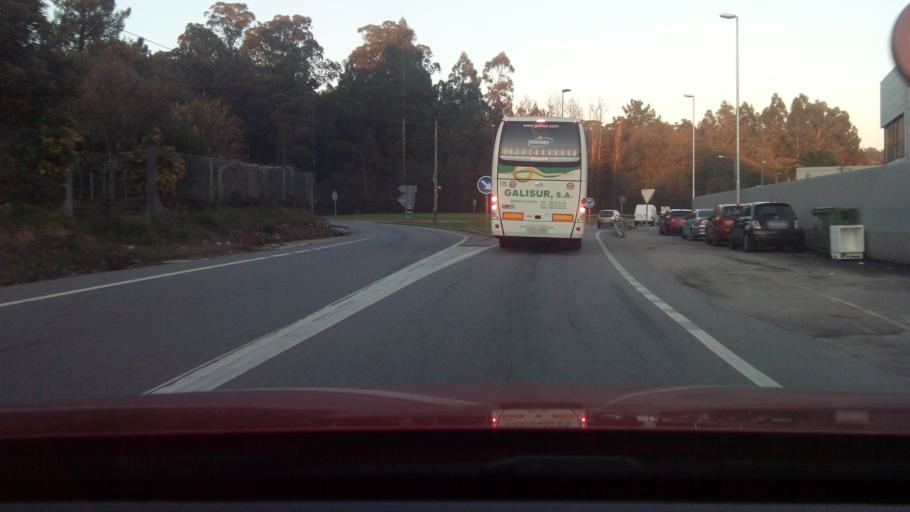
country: ES
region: Galicia
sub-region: Provincia de Pontevedra
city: Gondomar
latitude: 42.1565
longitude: -8.7168
